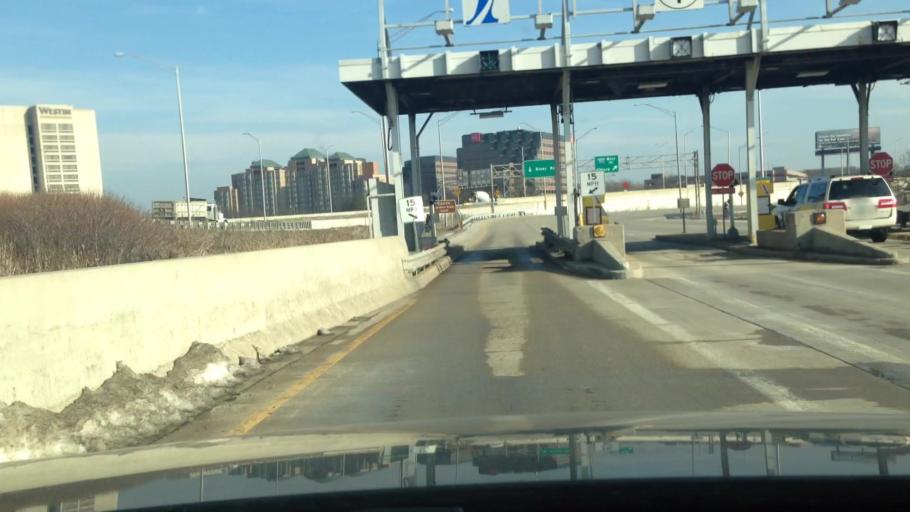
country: US
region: Illinois
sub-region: Cook County
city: Rosemont
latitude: 41.9868
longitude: -87.8645
